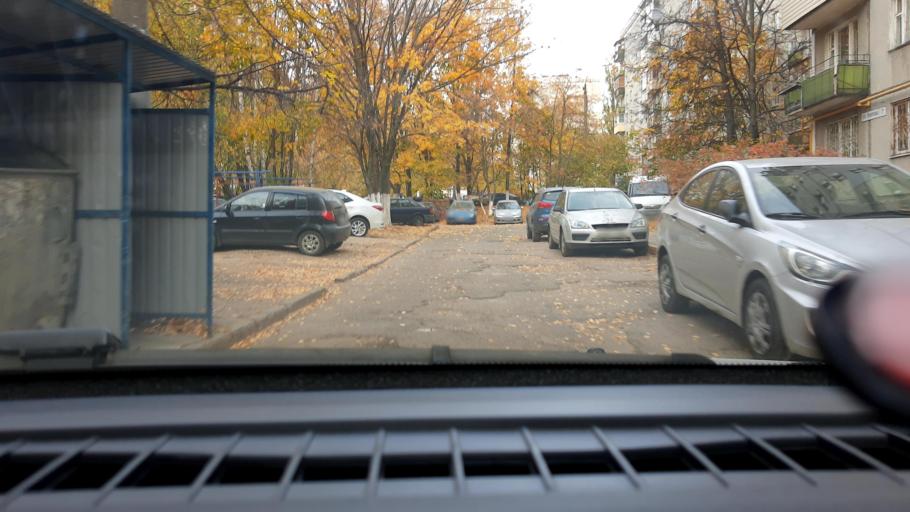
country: RU
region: Nizjnij Novgorod
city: Nizhniy Novgorod
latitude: 56.3121
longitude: 44.0477
